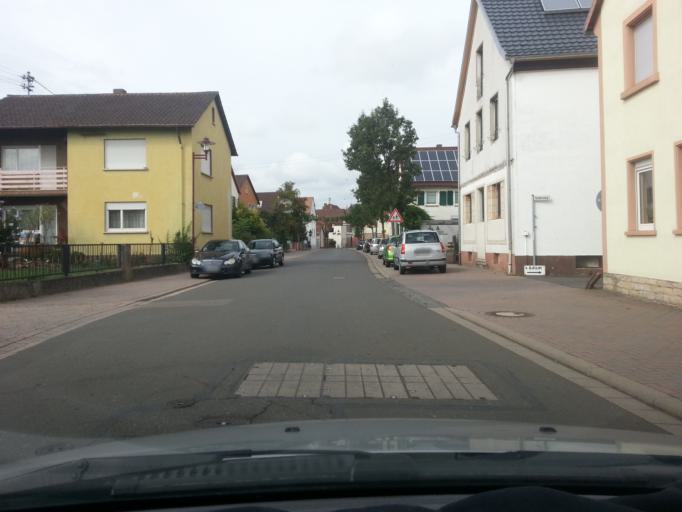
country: DE
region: Rheinland-Pfalz
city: Kirrweiler
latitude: 49.2993
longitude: 8.1669
